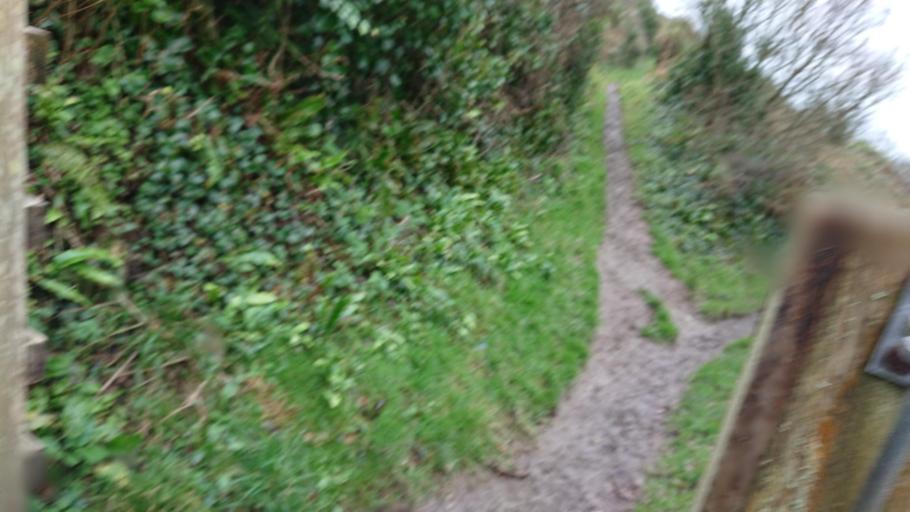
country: GB
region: England
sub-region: Cornwall
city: Fowey
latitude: 50.3337
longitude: -4.5771
